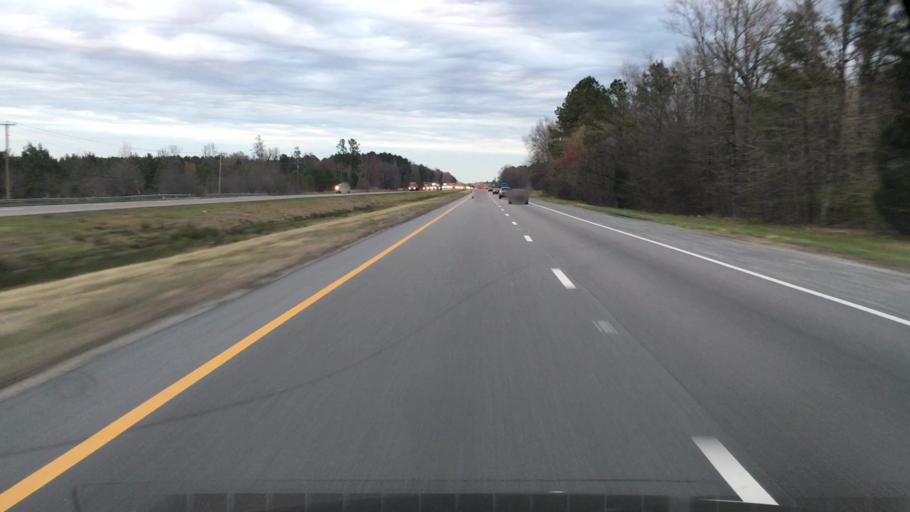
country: US
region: Virginia
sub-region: Sussex County
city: Sussex
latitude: 36.9136
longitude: -77.3975
